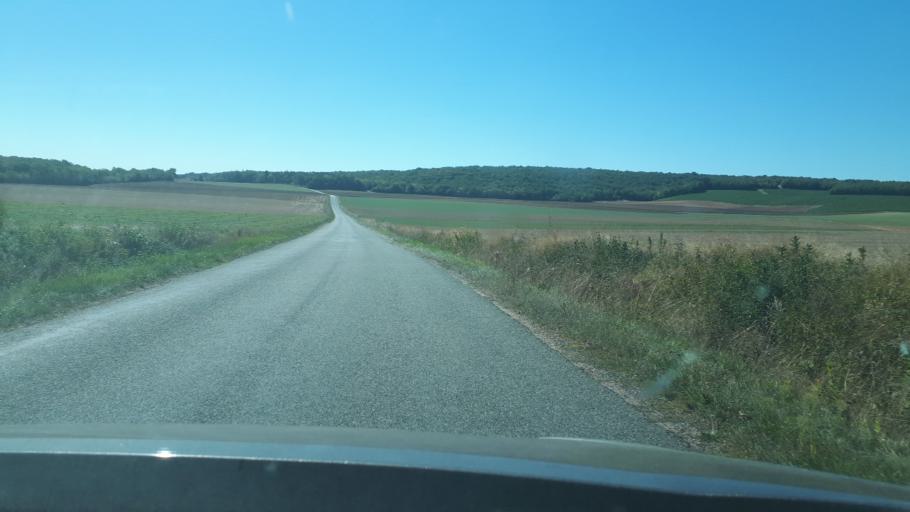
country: FR
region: Centre
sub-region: Departement du Cher
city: Sancerre
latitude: 47.2831
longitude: 2.7740
